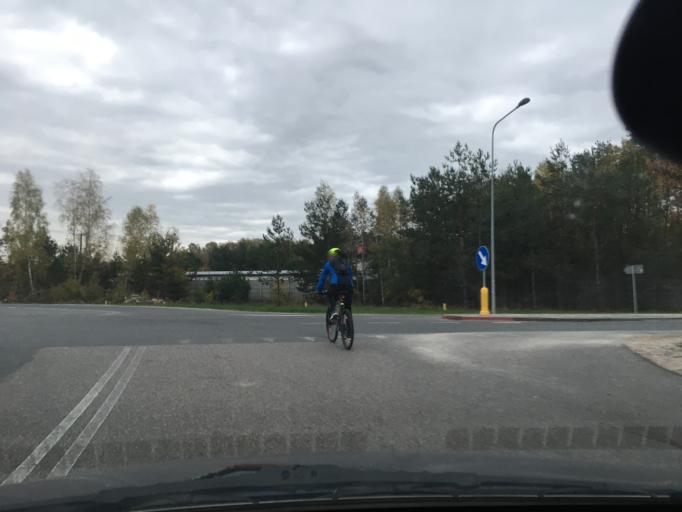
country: PL
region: Lodz Voivodeship
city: Zabia Wola
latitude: 52.0488
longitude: 20.7213
